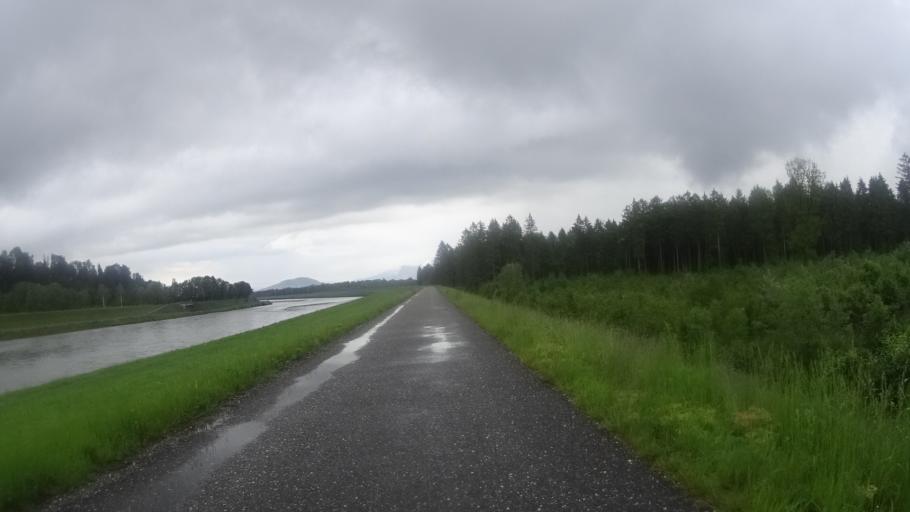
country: CH
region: Saint Gallen
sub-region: Wahlkreis Rheintal
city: Ruthi
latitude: 47.2751
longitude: 9.5397
